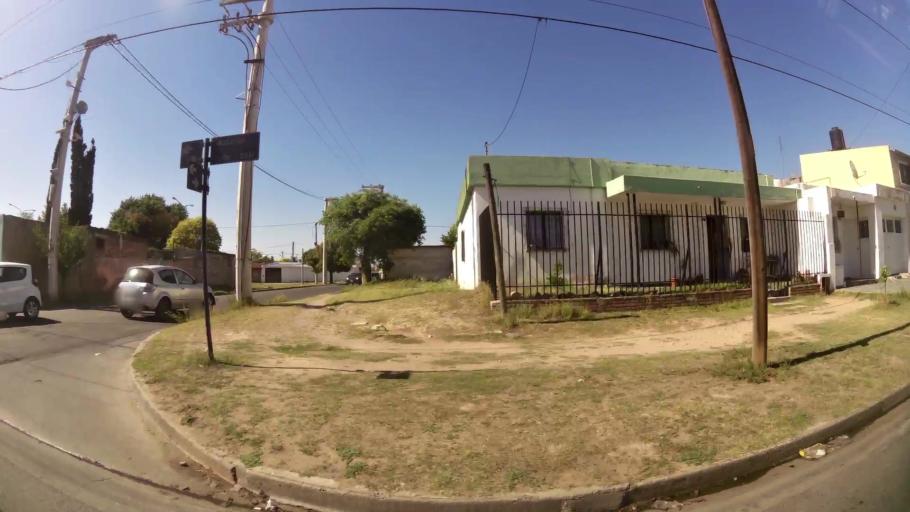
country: AR
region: Cordoba
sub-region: Departamento de Capital
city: Cordoba
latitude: -31.4354
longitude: -64.1416
